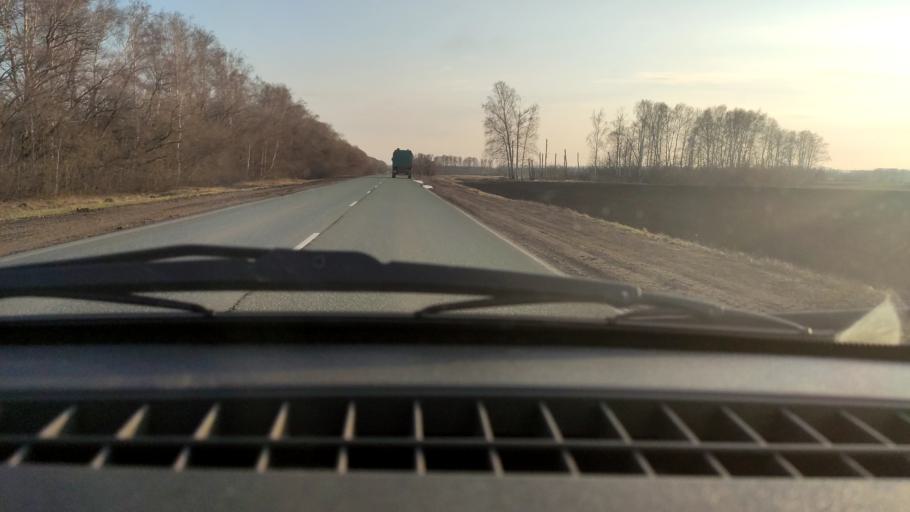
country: RU
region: Bashkortostan
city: Chishmy
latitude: 54.5424
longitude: 55.3203
